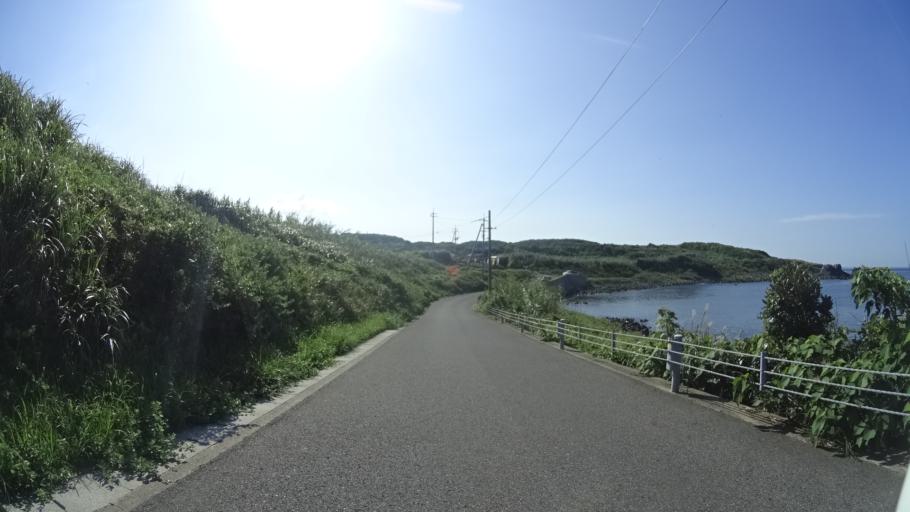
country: JP
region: Yamaguchi
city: Nagato
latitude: 34.3508
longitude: 130.8393
